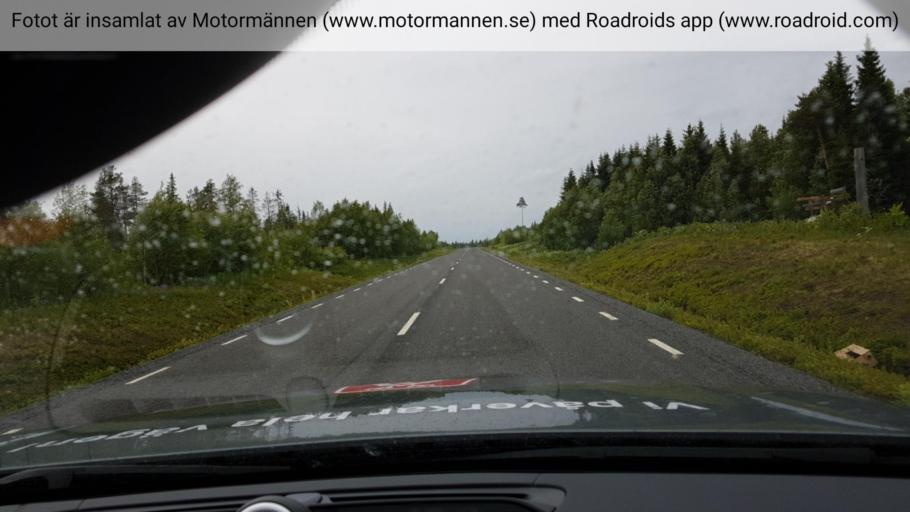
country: SE
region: Jaemtland
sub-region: Stroemsunds Kommun
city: Stroemsund
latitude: 63.6407
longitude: 15.1855
